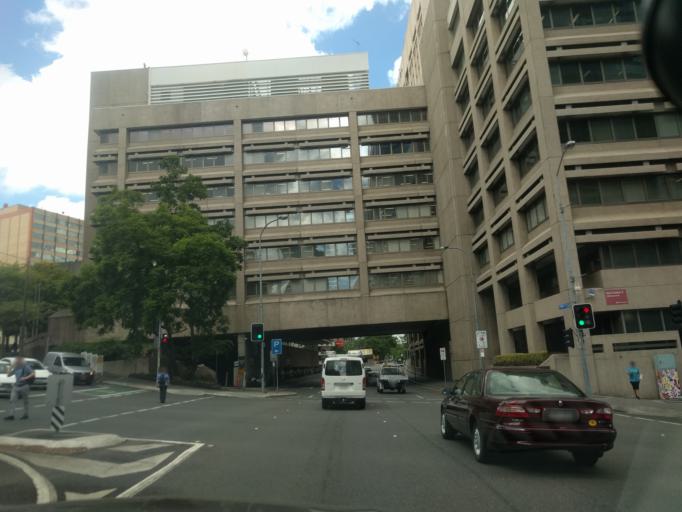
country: AU
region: Queensland
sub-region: Brisbane
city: Brisbane
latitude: -27.4662
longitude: 153.0245
